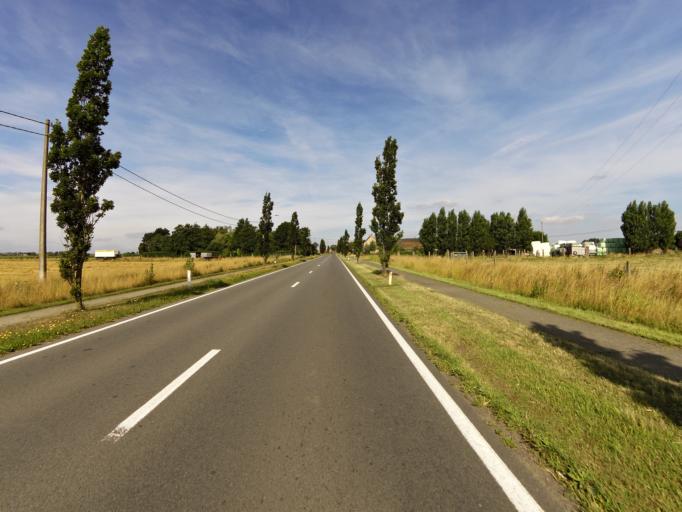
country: BE
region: Flanders
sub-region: Provincie West-Vlaanderen
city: Houthulst
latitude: 51.0210
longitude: 2.9323
